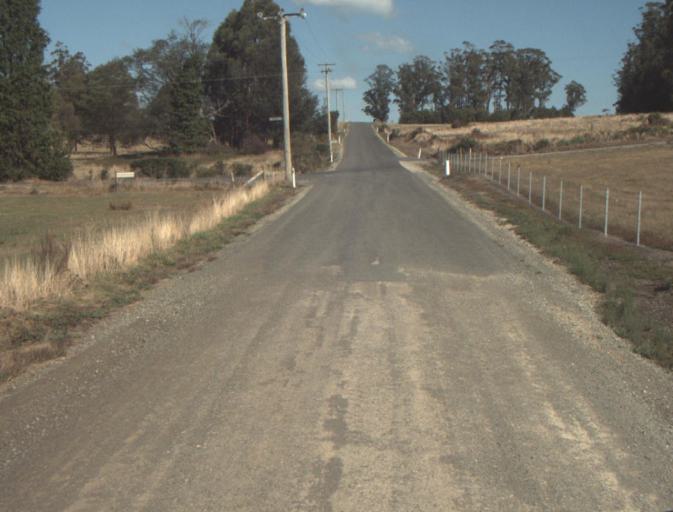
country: AU
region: Tasmania
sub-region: Launceston
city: Mayfield
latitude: -41.2301
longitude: 147.2356
